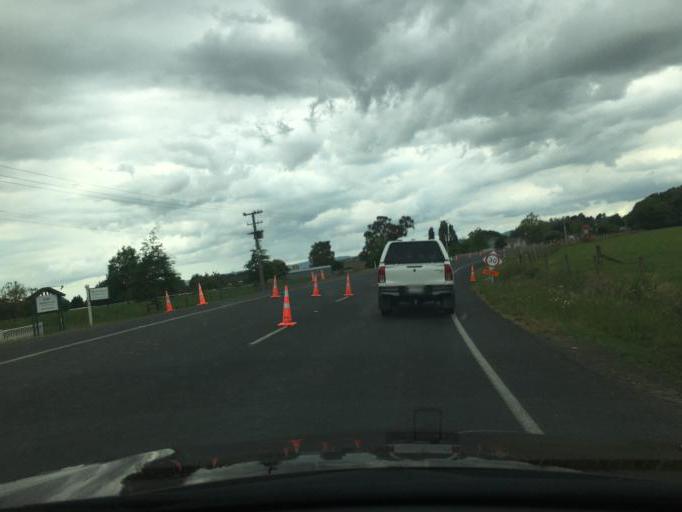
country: NZ
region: Waikato
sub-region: Waipa District
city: Cambridge
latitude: -37.9193
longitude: 175.4381
